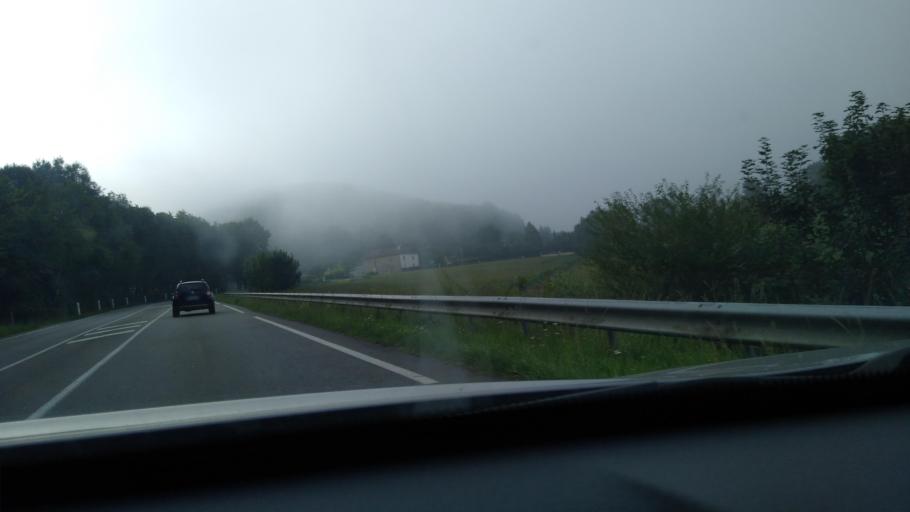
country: FR
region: Midi-Pyrenees
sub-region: Departement de la Haute-Garonne
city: Salies-du-Salat
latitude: 43.1175
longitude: 0.9346
